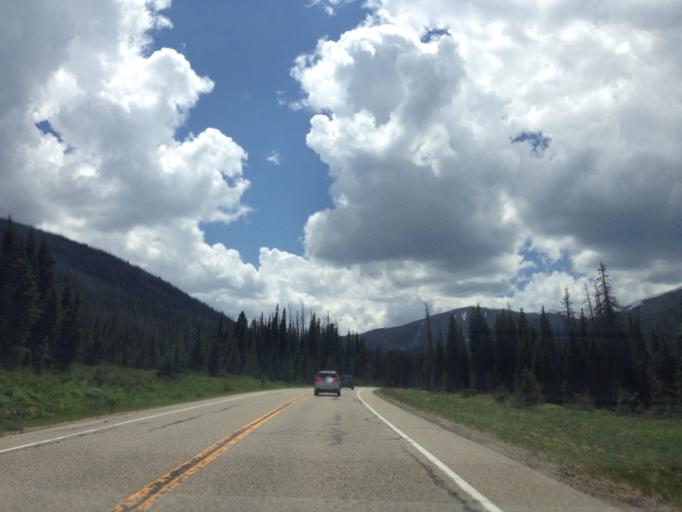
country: US
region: Colorado
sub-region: Larimer County
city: Estes Park
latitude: 40.5370
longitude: -105.8841
